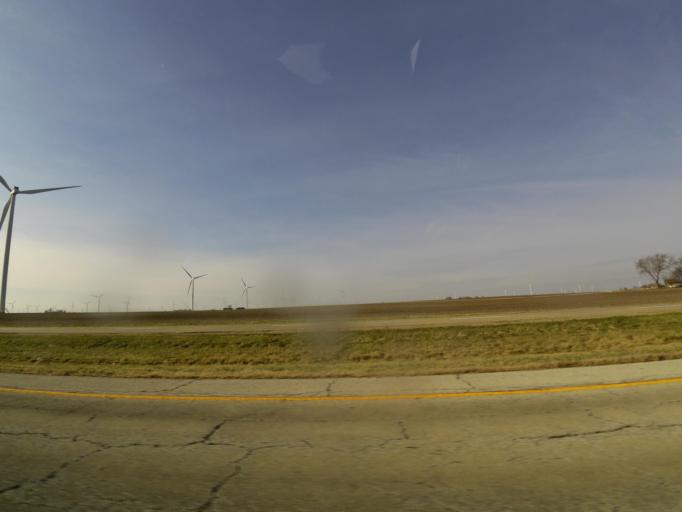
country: US
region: Illinois
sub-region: Macon County
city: Maroa
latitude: 40.0053
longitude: -88.9561
